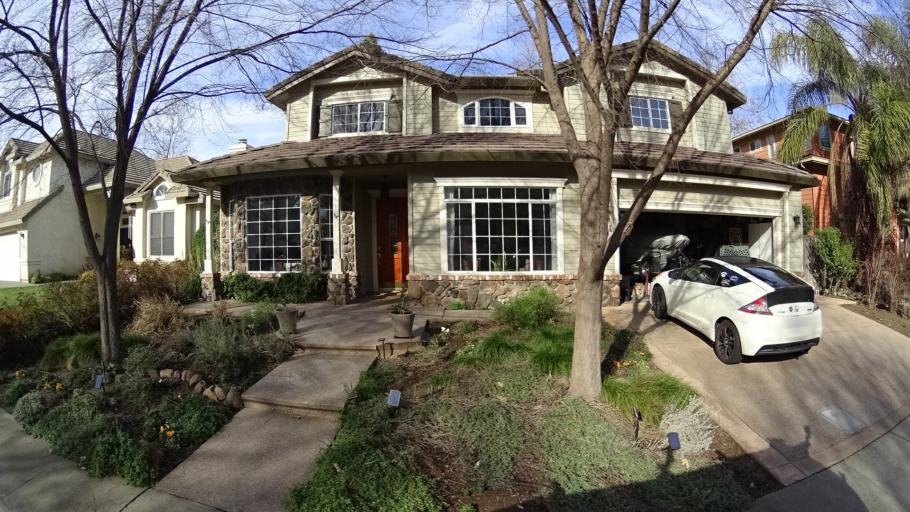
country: US
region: California
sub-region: Yolo County
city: Davis
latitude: 38.5461
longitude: -121.7045
